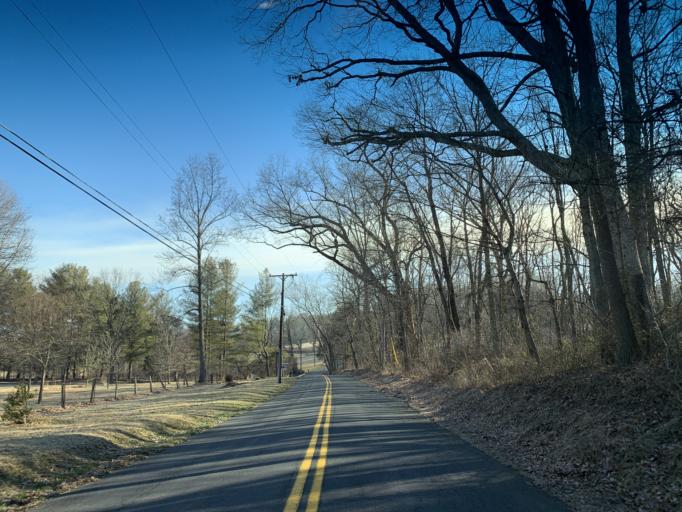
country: US
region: Maryland
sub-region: Harford County
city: Aberdeen
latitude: 39.6058
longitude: -76.2196
